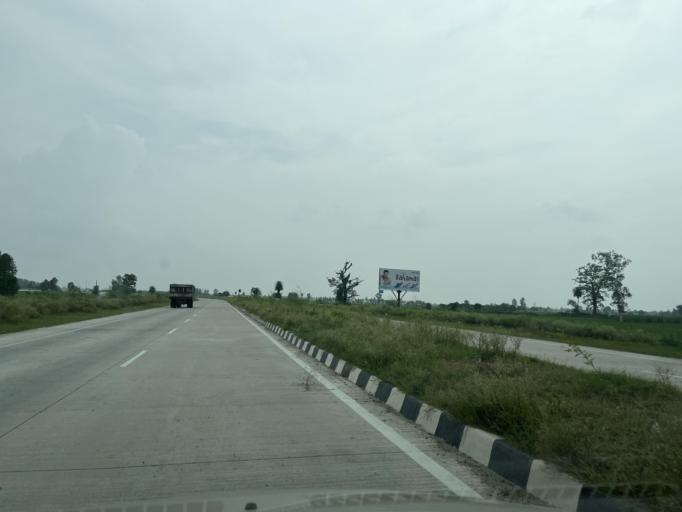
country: IN
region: Uttarakhand
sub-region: Udham Singh Nagar
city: Kashipur
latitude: 29.1817
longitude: 78.9394
